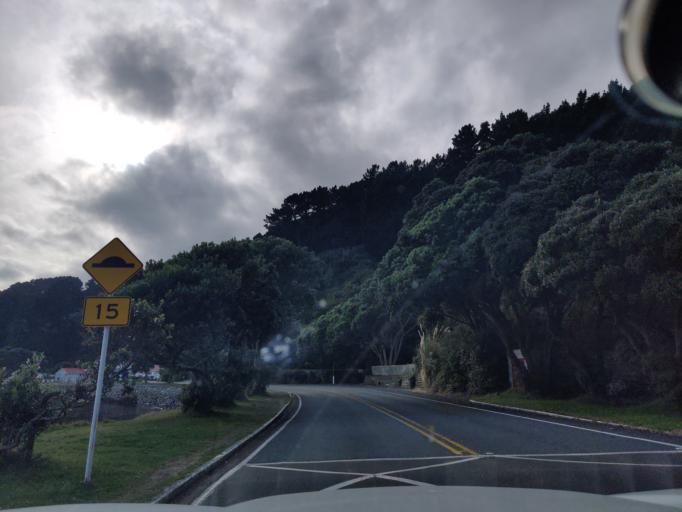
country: NZ
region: Wellington
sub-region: Wellington City
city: Wellington
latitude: -41.2971
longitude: 174.8216
